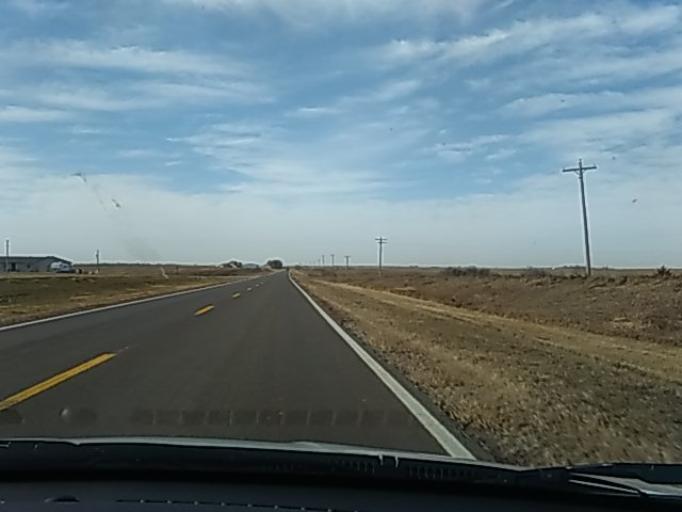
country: US
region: Nebraska
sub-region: Clay County
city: Clay Center
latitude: 40.4232
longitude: -97.9742
